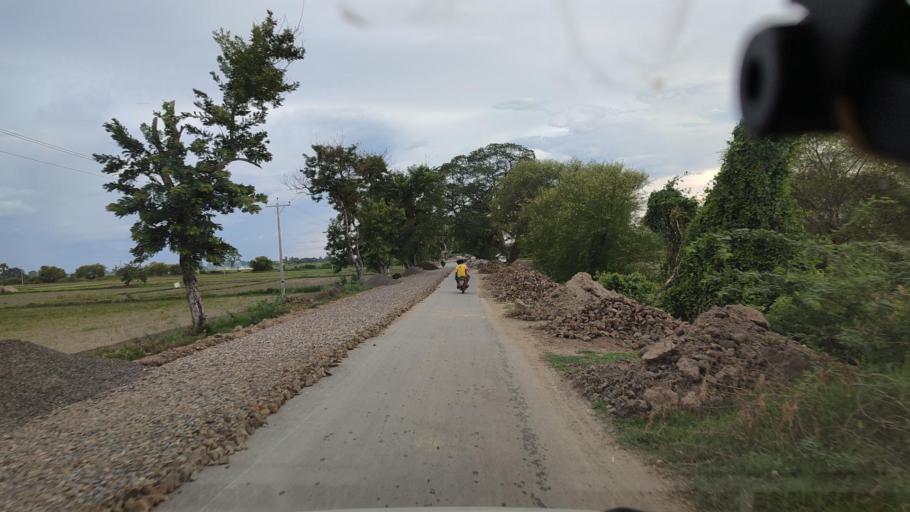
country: MM
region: Magway
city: Minbu
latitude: 20.3163
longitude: 94.7579
